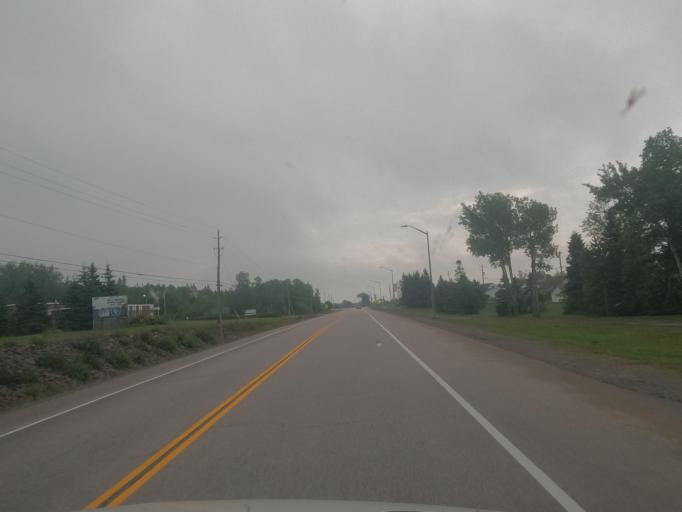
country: CA
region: Ontario
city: Marathon
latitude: 48.7836
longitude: -87.1095
